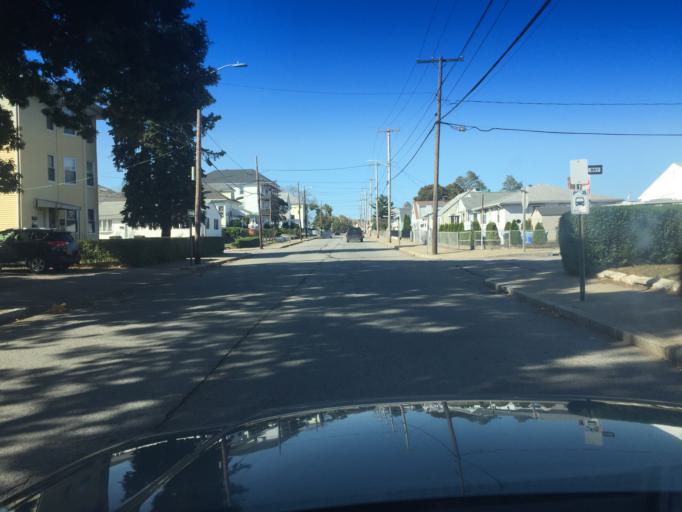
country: US
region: Rhode Island
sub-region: Providence County
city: Pawtucket
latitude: 41.8646
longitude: -71.3724
